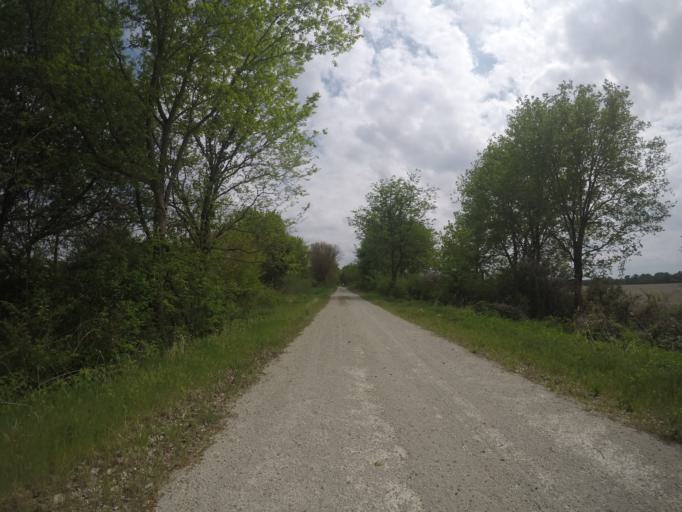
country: US
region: Kansas
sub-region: Marshall County
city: Marysville
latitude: 39.9833
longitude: -96.6027
